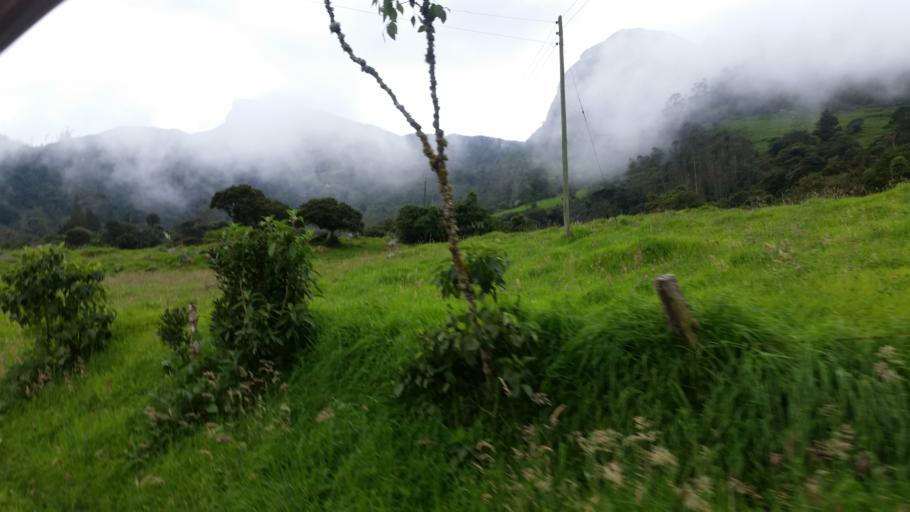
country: CO
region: Cundinamarca
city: Choachi
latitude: 4.5684
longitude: -73.9491
